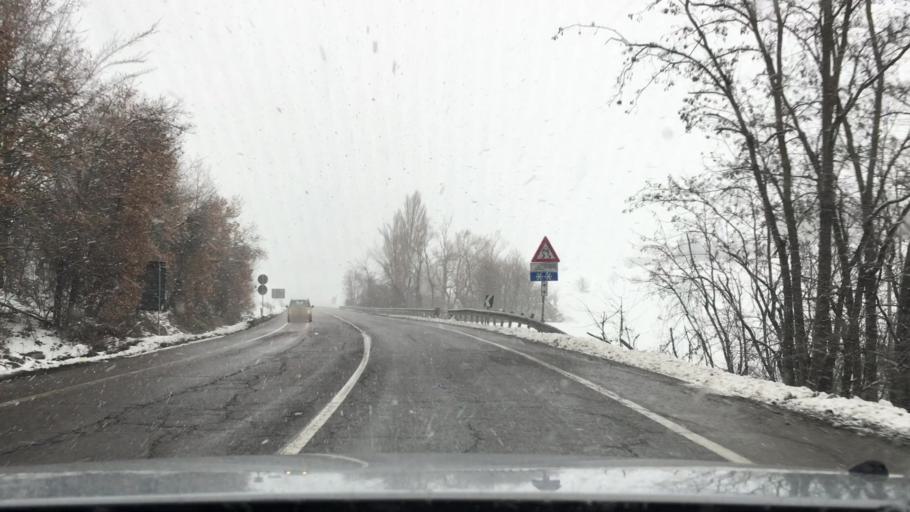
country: IT
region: Emilia-Romagna
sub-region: Provincia di Modena
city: Sant'Antonio
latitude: 44.4086
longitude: 10.8415
